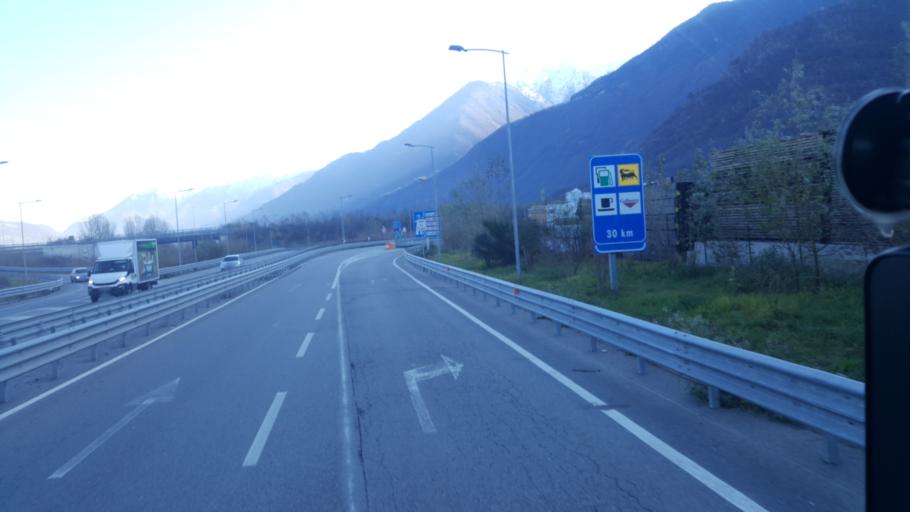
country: IT
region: Lombardy
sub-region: Provincia di Sondrio
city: Piantedo
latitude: 46.1435
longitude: 9.4082
